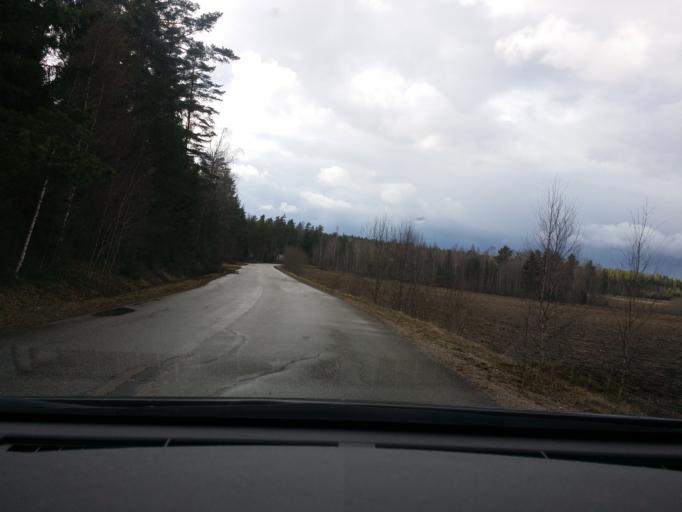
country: SE
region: Soedermanland
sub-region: Eskilstuna Kommun
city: Arla
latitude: 59.2995
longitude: 16.6857
